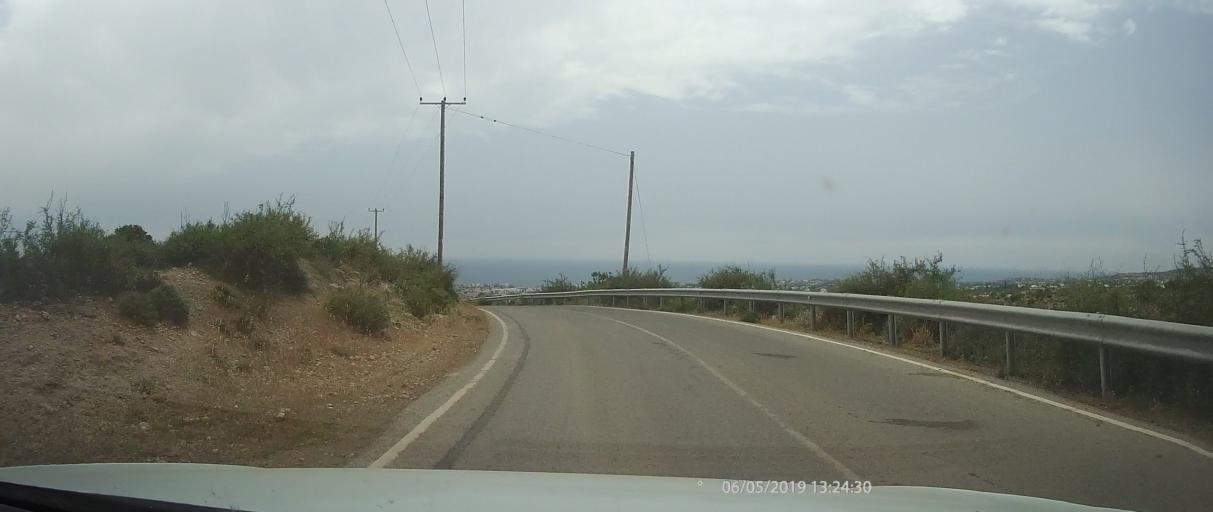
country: CY
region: Pafos
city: Pegeia
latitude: 34.8616
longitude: 32.3981
